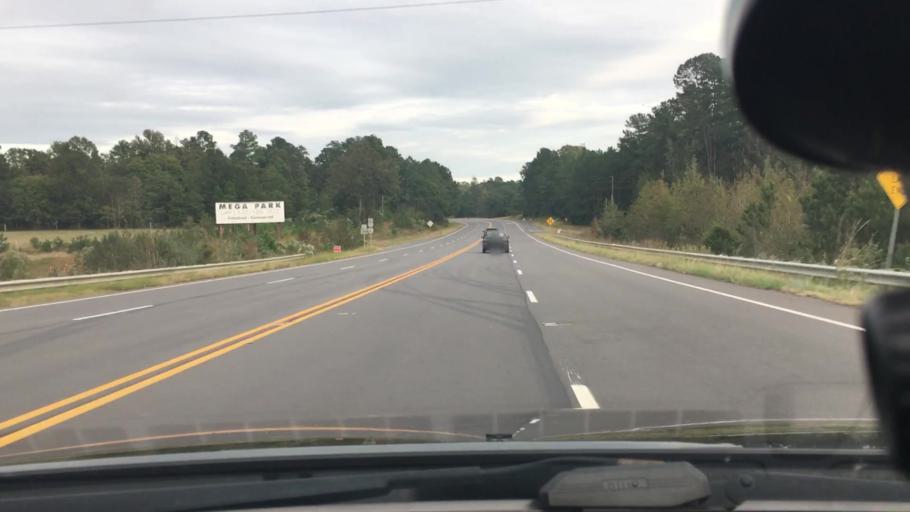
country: US
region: North Carolina
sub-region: Montgomery County
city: Biscoe
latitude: 35.3608
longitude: -79.7628
